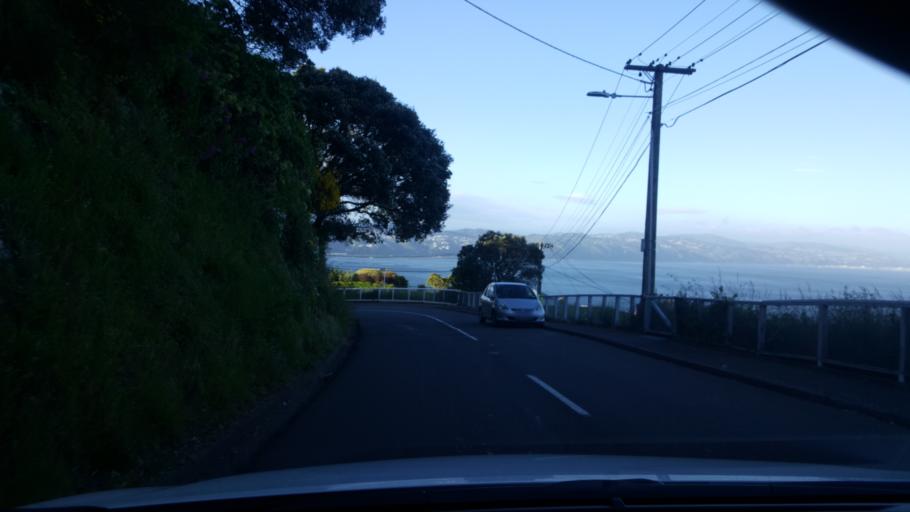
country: NZ
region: Wellington
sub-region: Wellington City
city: Wellington
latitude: -41.2938
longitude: 174.7991
